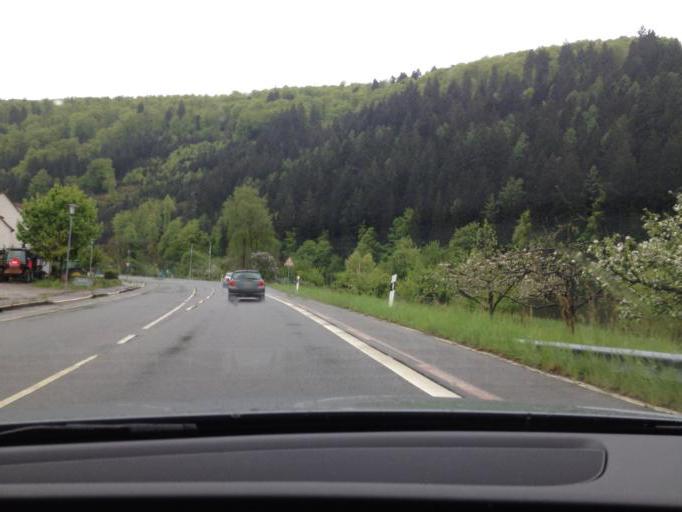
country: DE
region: Baden-Wuerttemberg
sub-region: Karlsruhe Region
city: Neunkirchen
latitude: 49.4191
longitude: 9.0022
